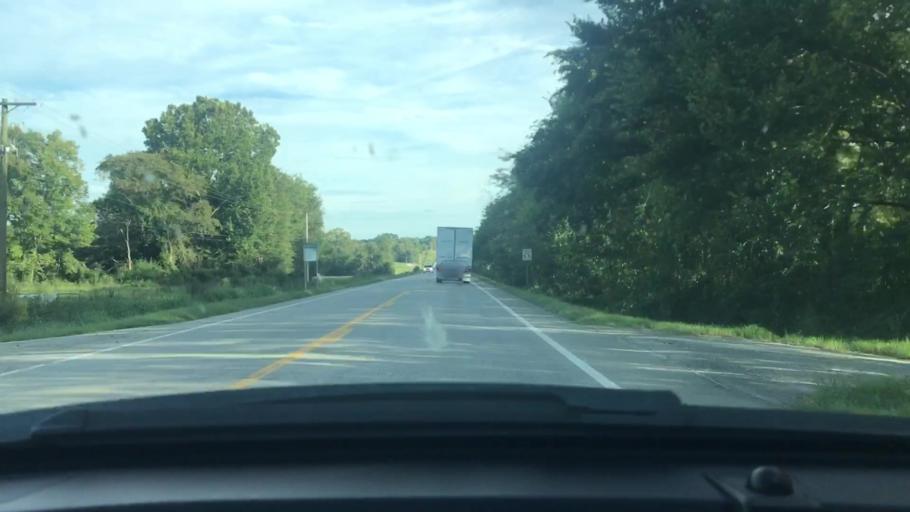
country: US
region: Arkansas
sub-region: Randolph County
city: Pocahontas
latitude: 36.1963
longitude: -91.1679
